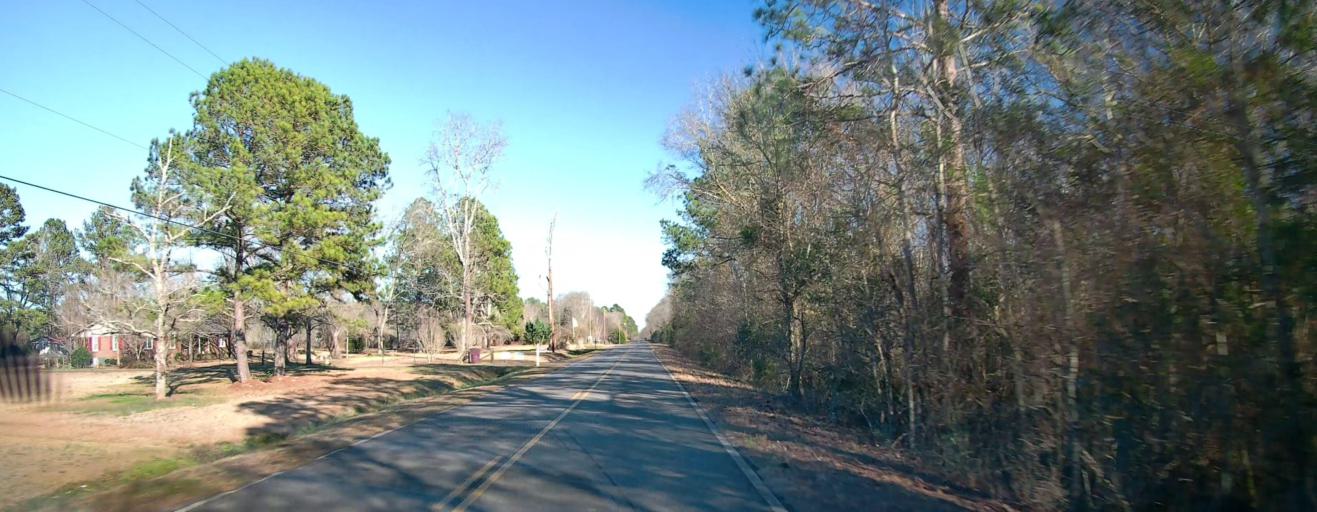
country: US
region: Georgia
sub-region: Sumter County
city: Americus
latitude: 32.0469
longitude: -84.2680
